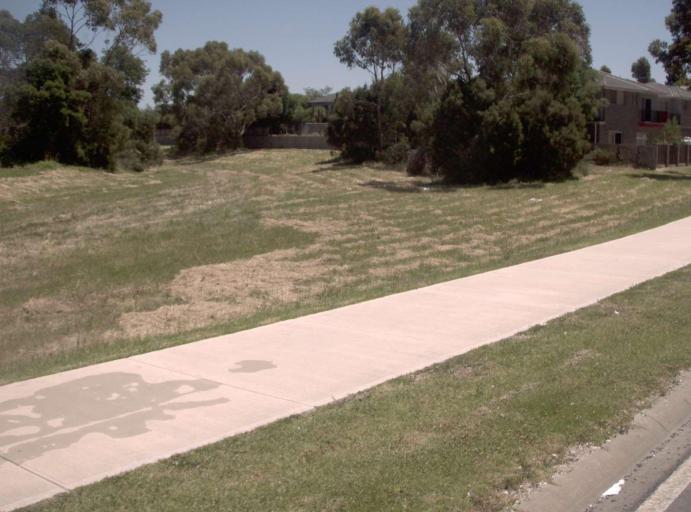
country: AU
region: Victoria
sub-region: Casey
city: Narre Warren
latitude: -38.0178
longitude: 145.2947
